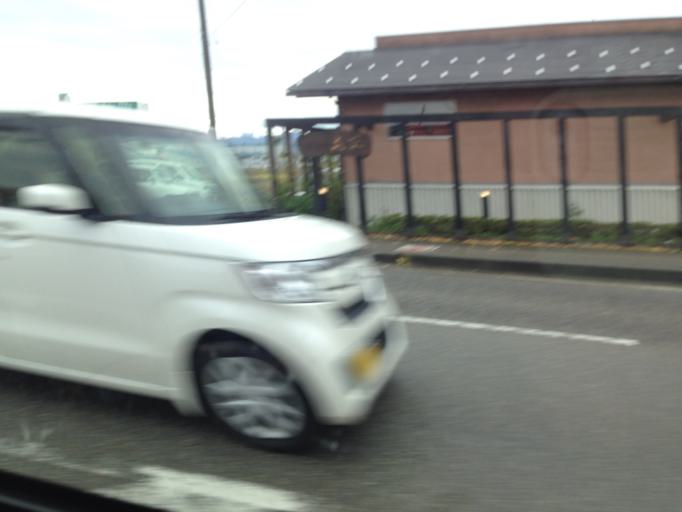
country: JP
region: Ishikawa
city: Komatsu
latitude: 36.3189
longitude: 136.3543
